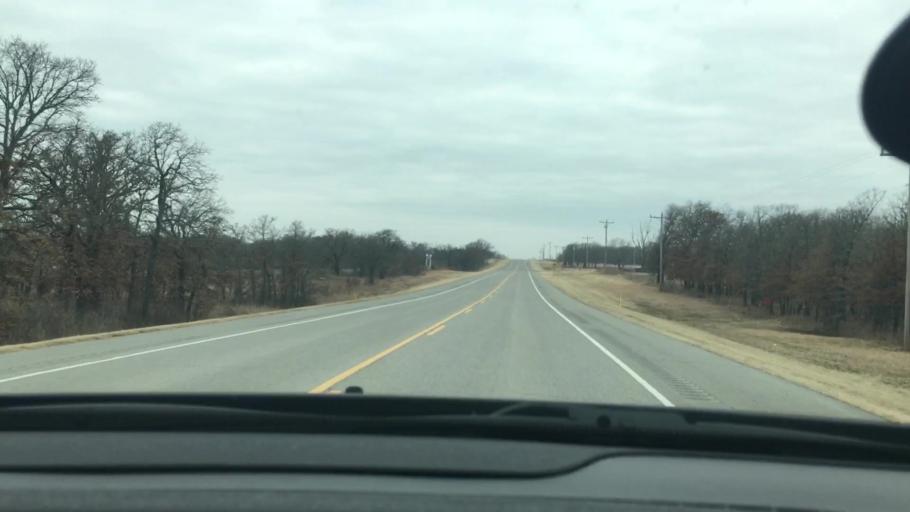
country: US
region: Oklahoma
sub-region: Carter County
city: Healdton
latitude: 34.4899
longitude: -97.4483
